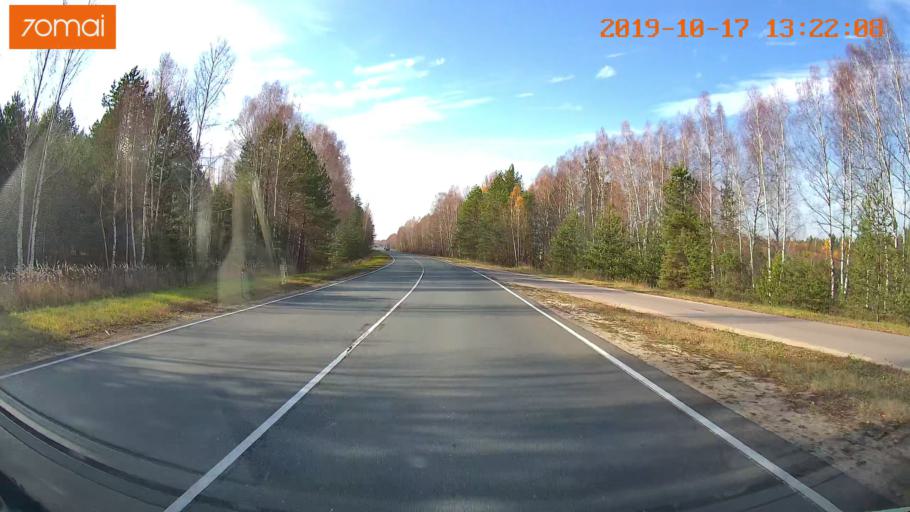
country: RU
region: Rjazan
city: Gus'-Zheleznyy
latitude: 55.0850
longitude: 41.0108
